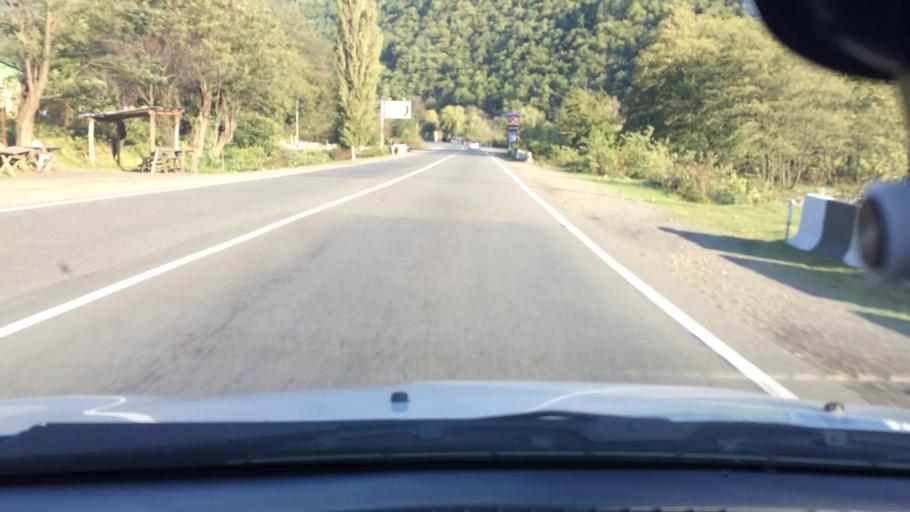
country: GE
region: Imereti
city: Kharagauli
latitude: 42.1053
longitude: 43.3405
